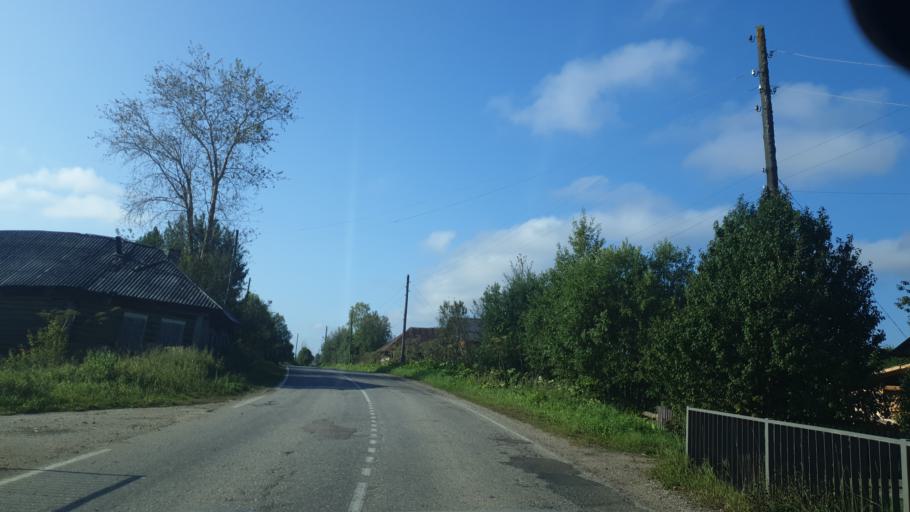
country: RU
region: Komi Republic
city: Vizinga
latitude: 60.9389
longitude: 50.2318
